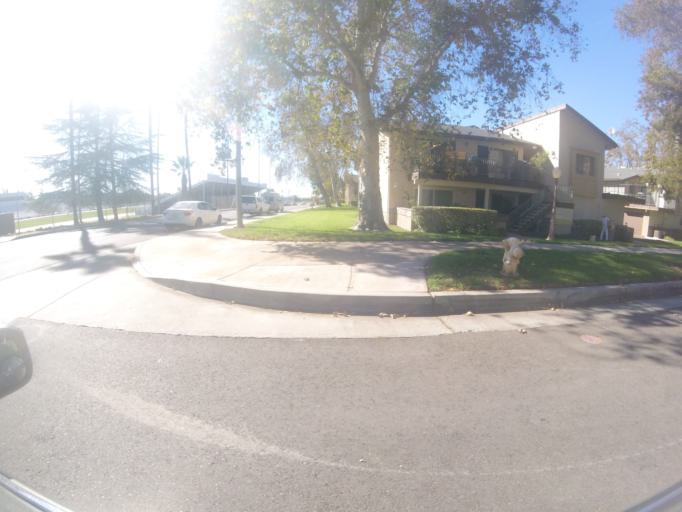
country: US
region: California
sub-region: San Bernardino County
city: Redlands
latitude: 34.0684
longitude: -117.1640
